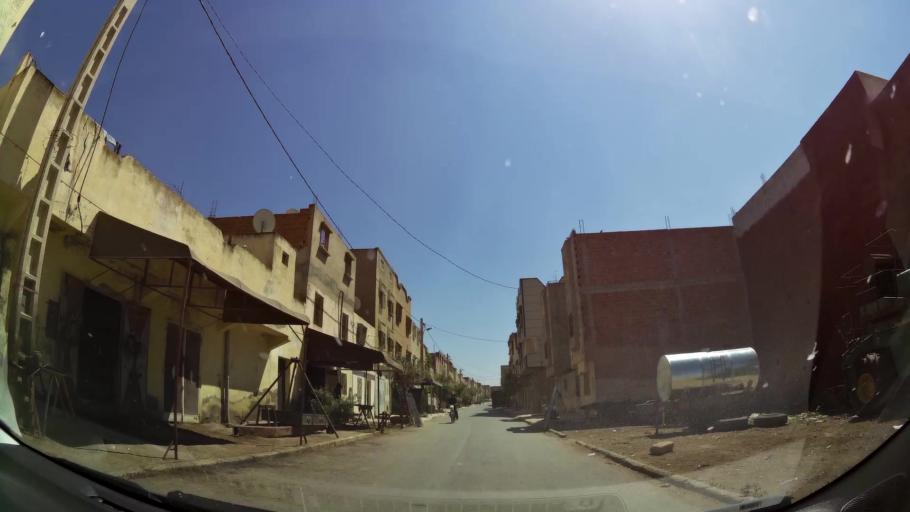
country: MA
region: Oriental
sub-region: Oujda-Angad
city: Oujda
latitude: 34.6902
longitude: -1.9324
